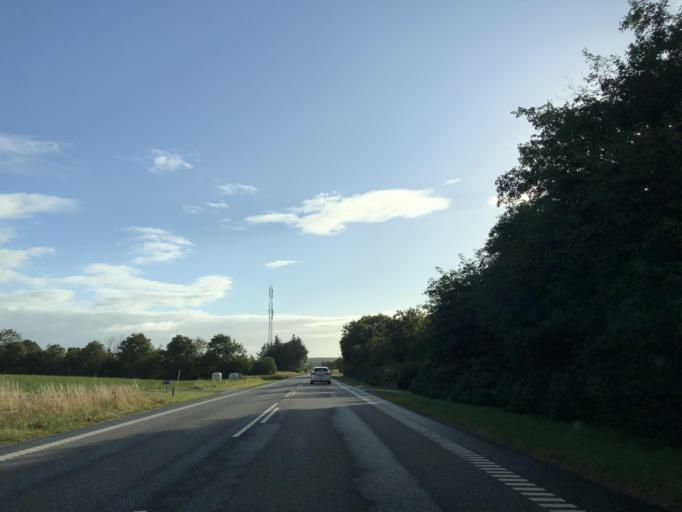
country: DK
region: Central Jutland
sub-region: Viborg Kommune
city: Stoholm
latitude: 56.4403
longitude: 9.1682
